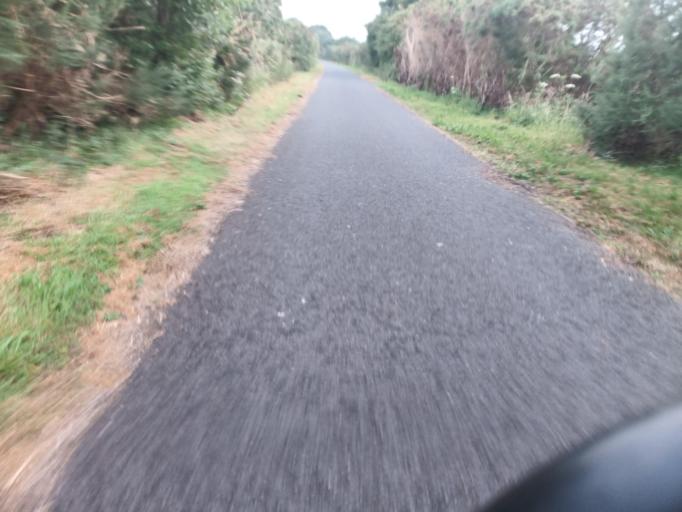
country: GB
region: Northern Ireland
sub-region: Ards District
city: Comber
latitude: 54.5648
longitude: -5.7640
